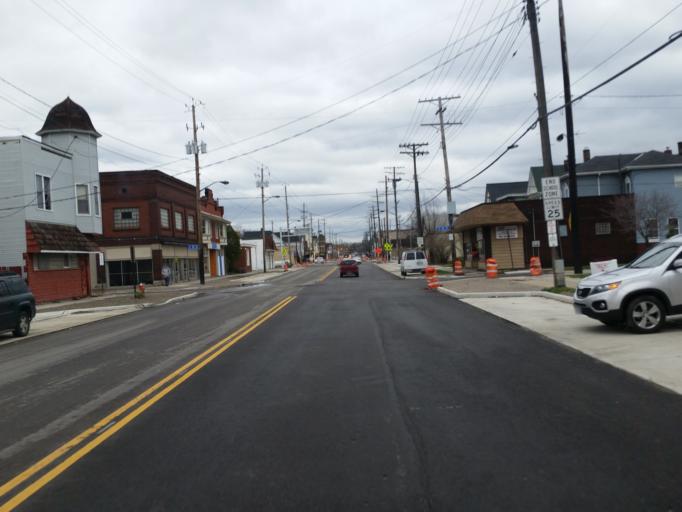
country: US
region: Ohio
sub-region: Cuyahoga County
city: Newburgh Heights
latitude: 41.4559
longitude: -81.6550
